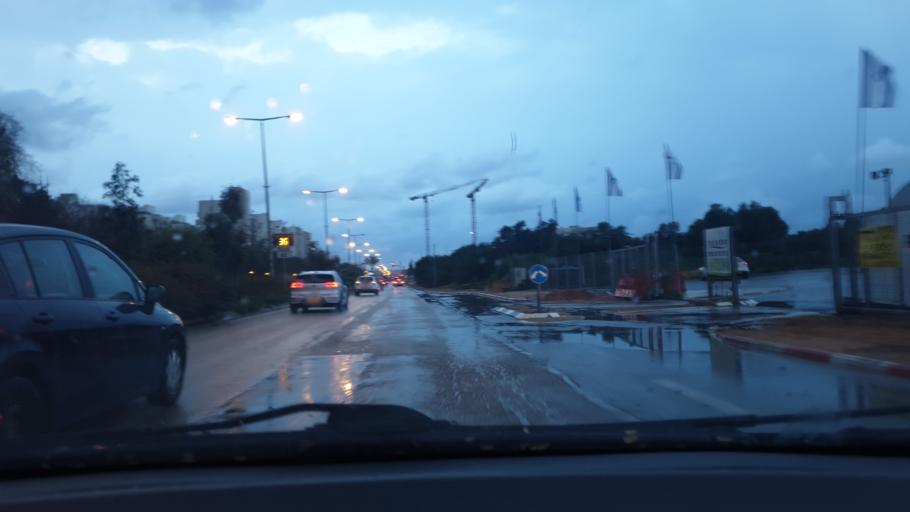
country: IL
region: Central District
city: Bet Dagan
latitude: 31.9730
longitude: 34.8196
